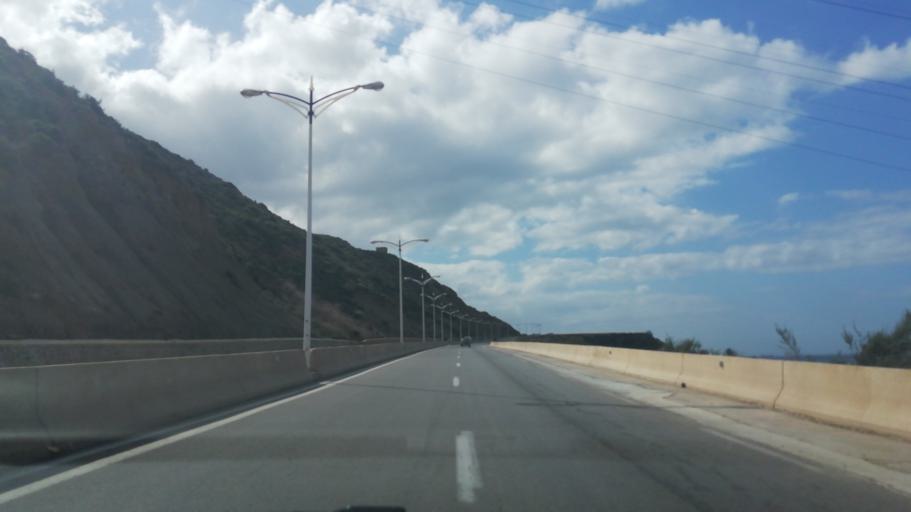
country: DZ
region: Mostaganem
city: Mostaganem
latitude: 36.0128
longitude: 0.1301
